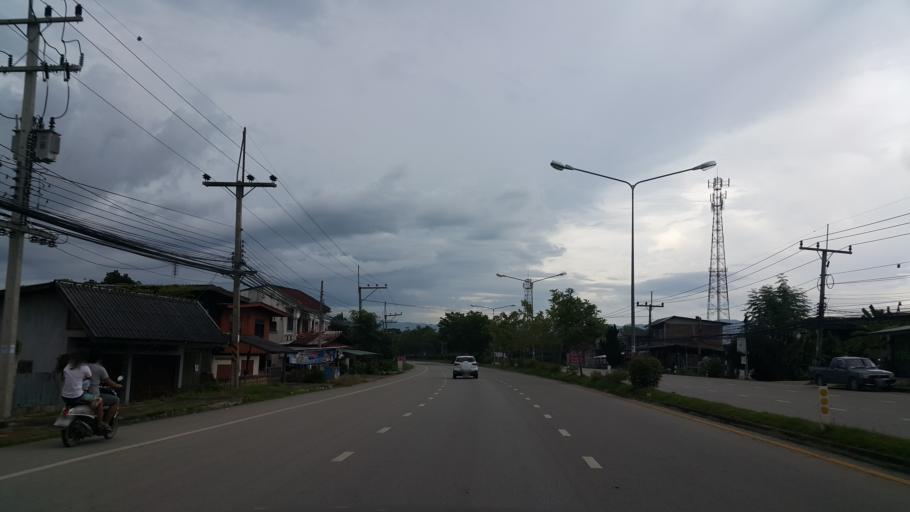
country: TH
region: Phayao
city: Dok Kham Tai
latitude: 19.1645
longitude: 99.9978
